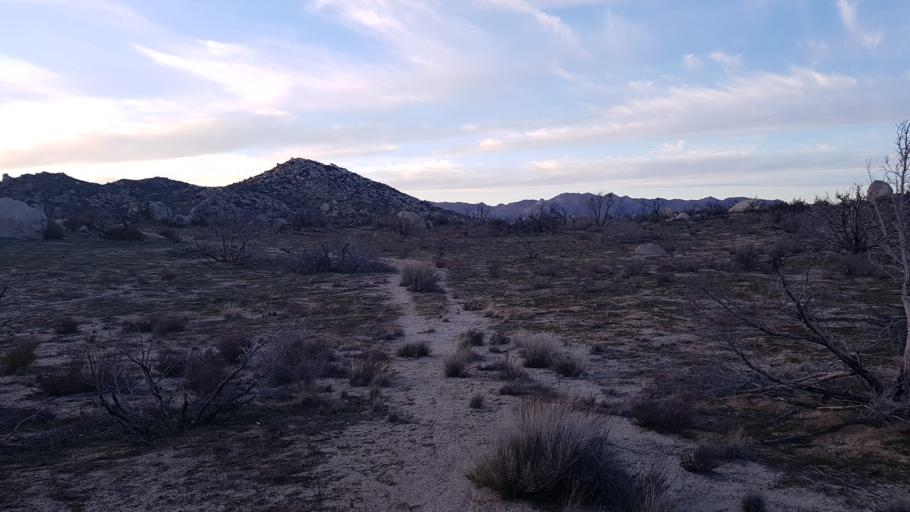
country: US
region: California
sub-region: San Diego County
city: Borrego Springs
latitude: 33.1781
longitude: -116.4442
